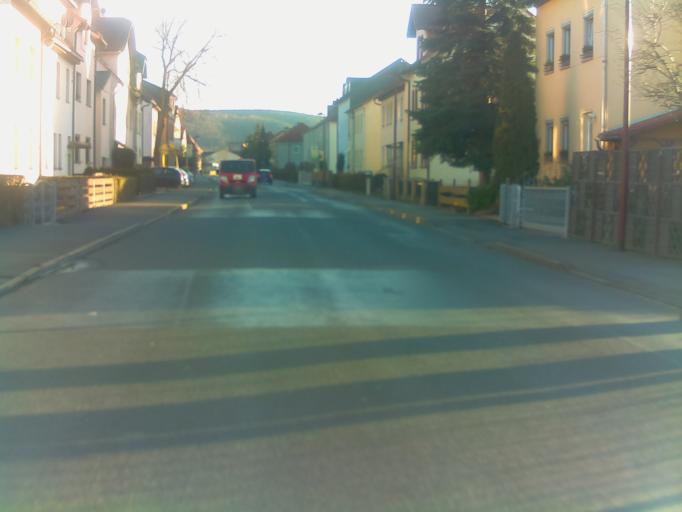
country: DE
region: Thuringia
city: Rudolstadt
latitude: 50.7035
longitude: 11.3254
